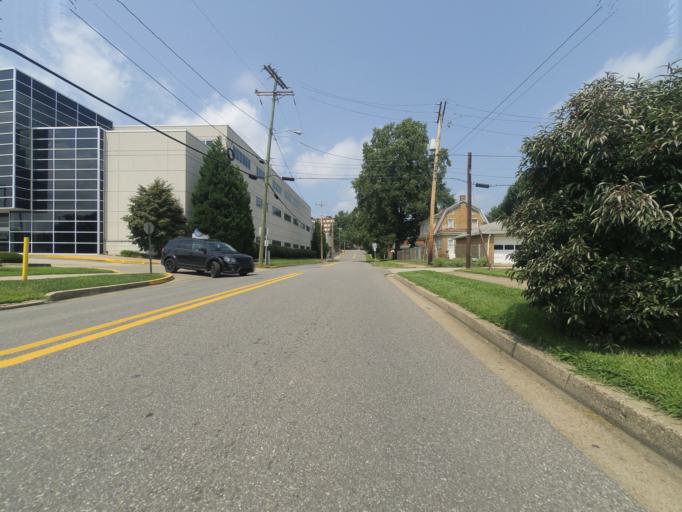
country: US
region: West Virginia
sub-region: Cabell County
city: Huntington
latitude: 38.4301
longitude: -82.3994
